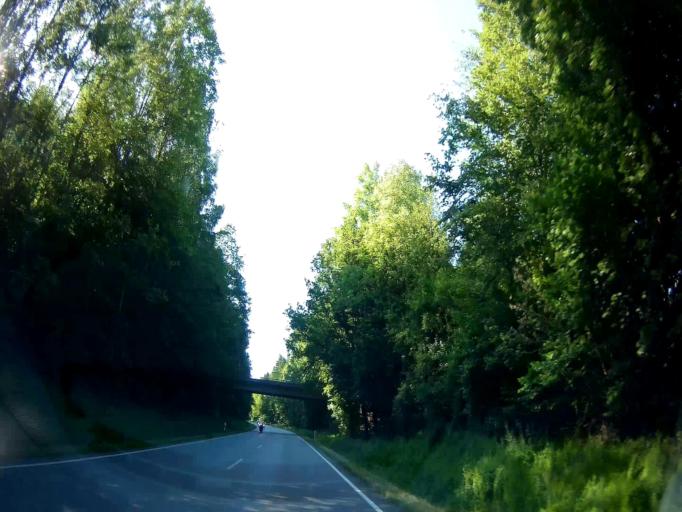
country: DE
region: Bavaria
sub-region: Lower Bavaria
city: Eggenfelden
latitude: 48.4109
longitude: 12.7778
